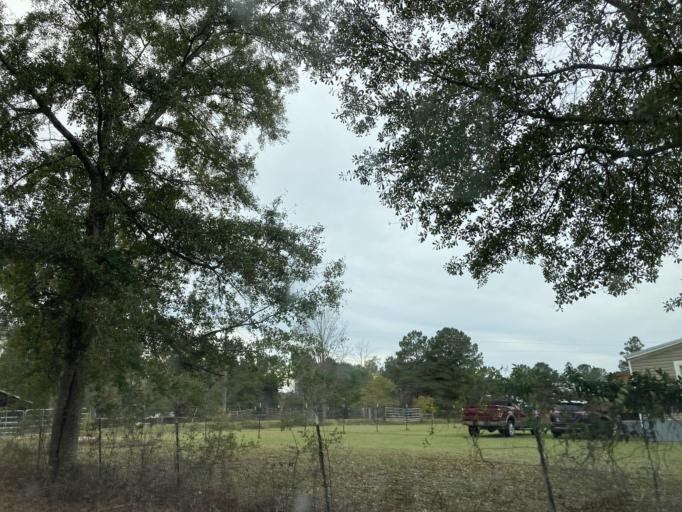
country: US
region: Mississippi
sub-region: Lamar County
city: Purvis
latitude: 31.0976
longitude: -89.4688
